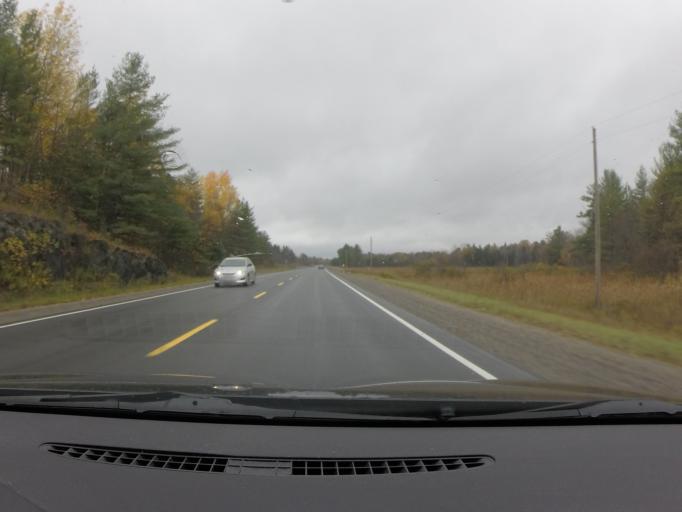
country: CA
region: Ontario
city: Belleville
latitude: 44.5444
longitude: -77.3419
